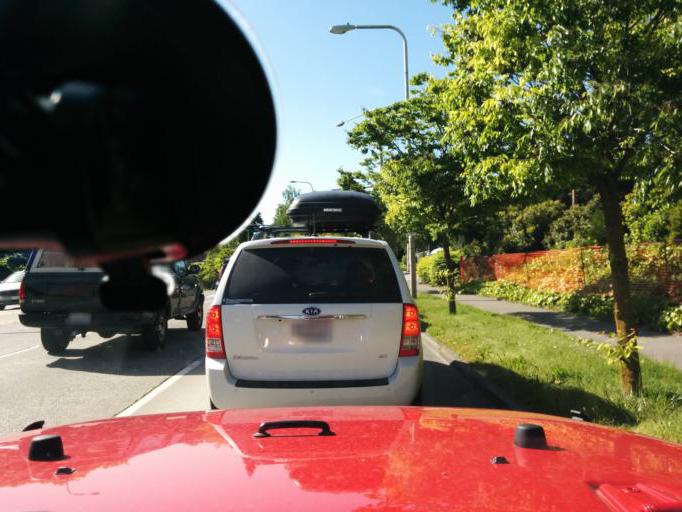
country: US
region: Washington
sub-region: King County
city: Seattle
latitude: 47.6533
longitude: -122.3129
